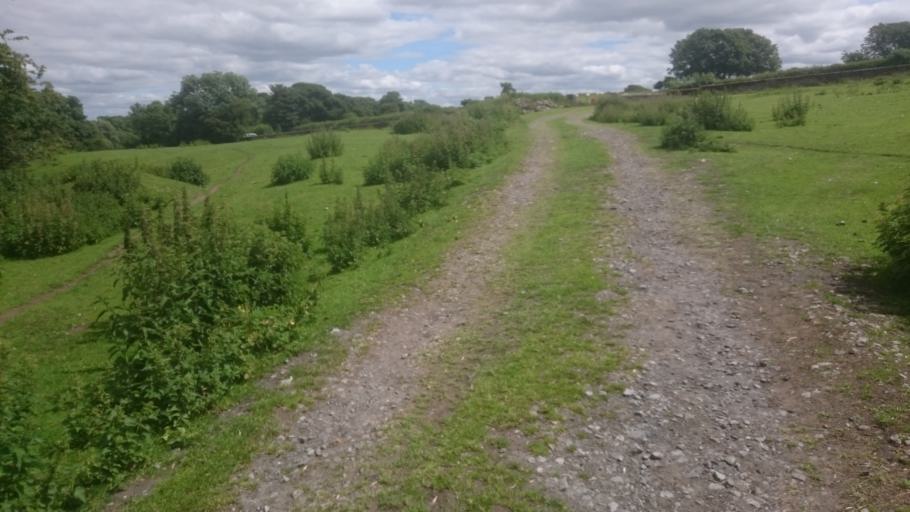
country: IE
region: Leinster
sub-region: Kilkenny
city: Kilkenny
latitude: 52.5377
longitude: -7.2651
